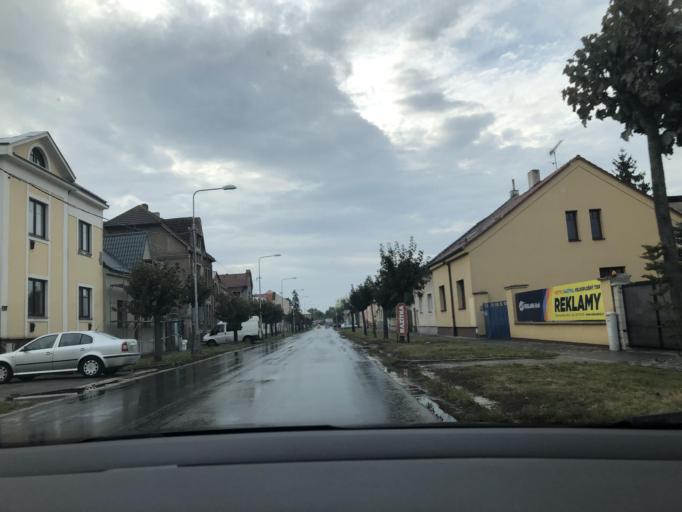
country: CZ
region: Central Bohemia
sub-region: Okres Kolin
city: Kolin
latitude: 50.0329
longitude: 15.2188
